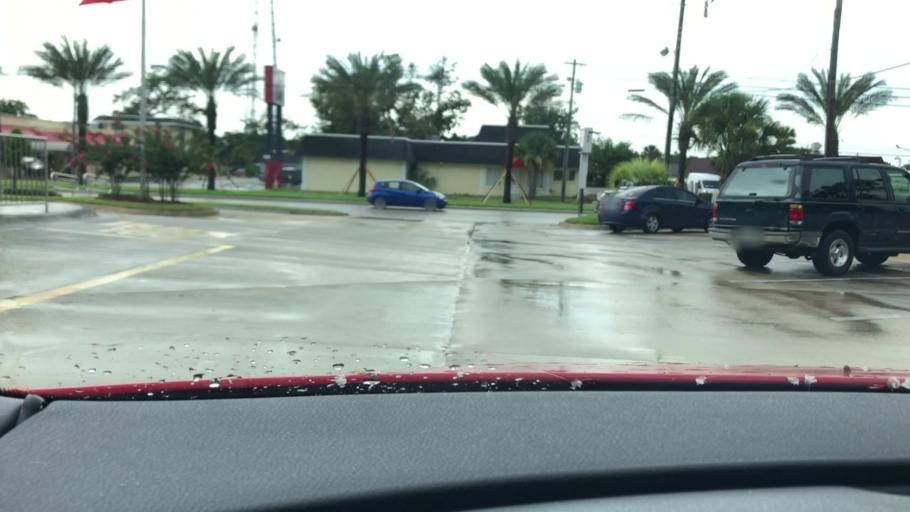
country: US
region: Florida
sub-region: Volusia County
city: Holly Hill
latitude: 29.2284
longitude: -81.0317
